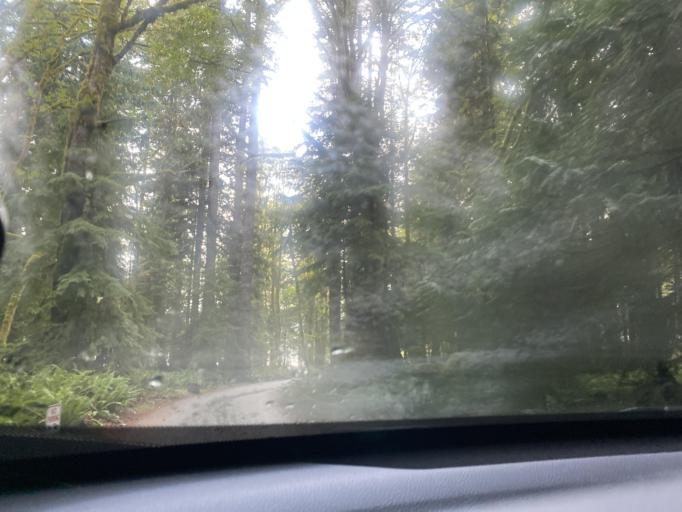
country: CA
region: British Columbia
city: Sooke
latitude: 48.0575
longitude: -123.7971
